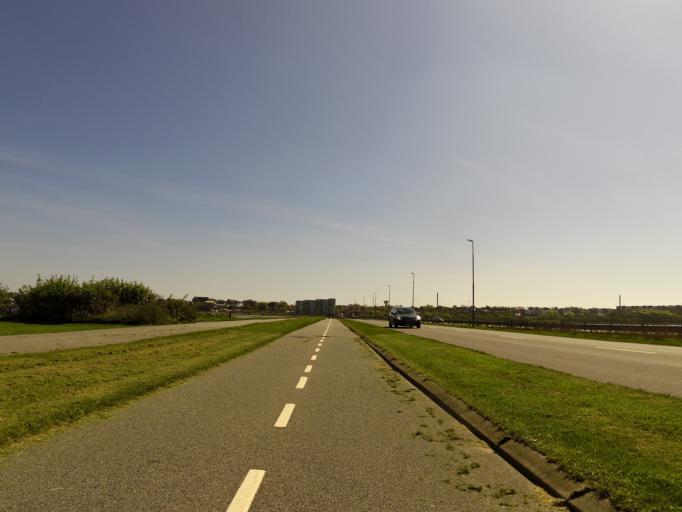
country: DK
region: Central Jutland
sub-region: Struer Kommune
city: Struer
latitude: 56.4999
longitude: 8.5825
